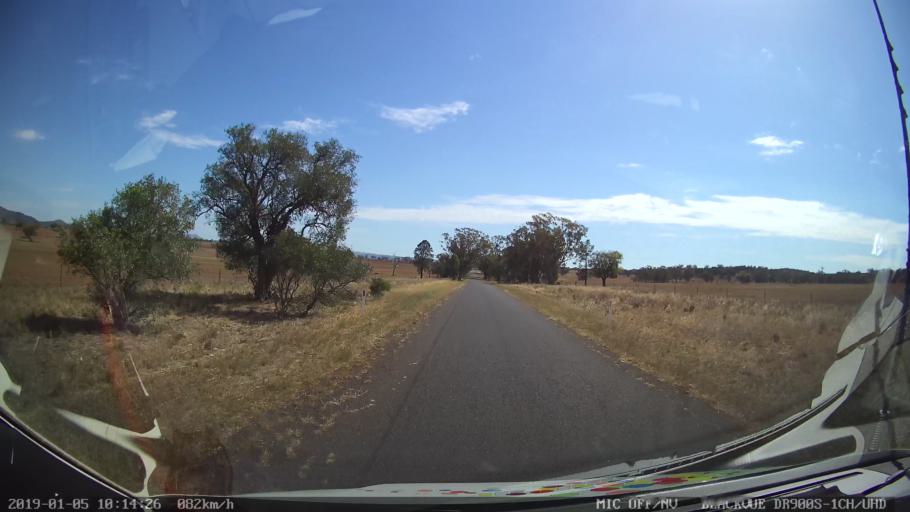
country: AU
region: New South Wales
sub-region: Gilgandra
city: Gilgandra
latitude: -31.5929
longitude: 148.9343
